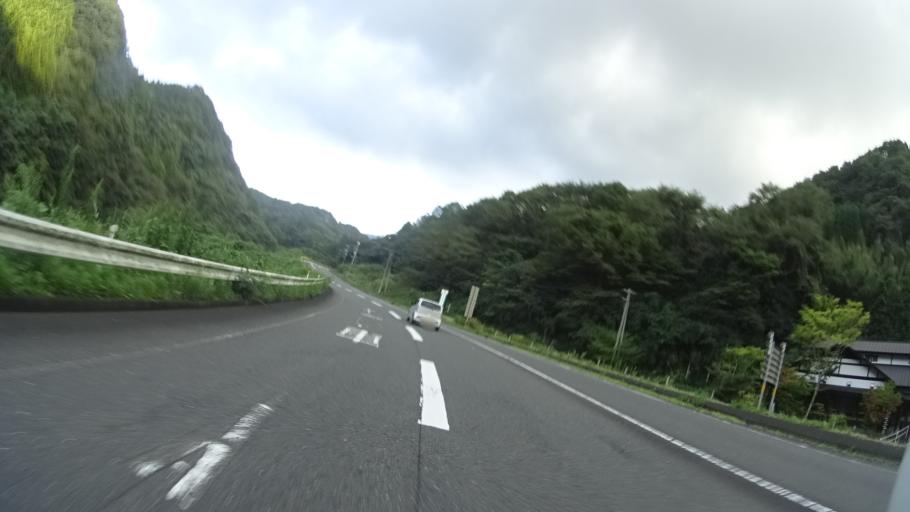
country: JP
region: Oita
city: Beppu
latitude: 33.3487
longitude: 131.4001
